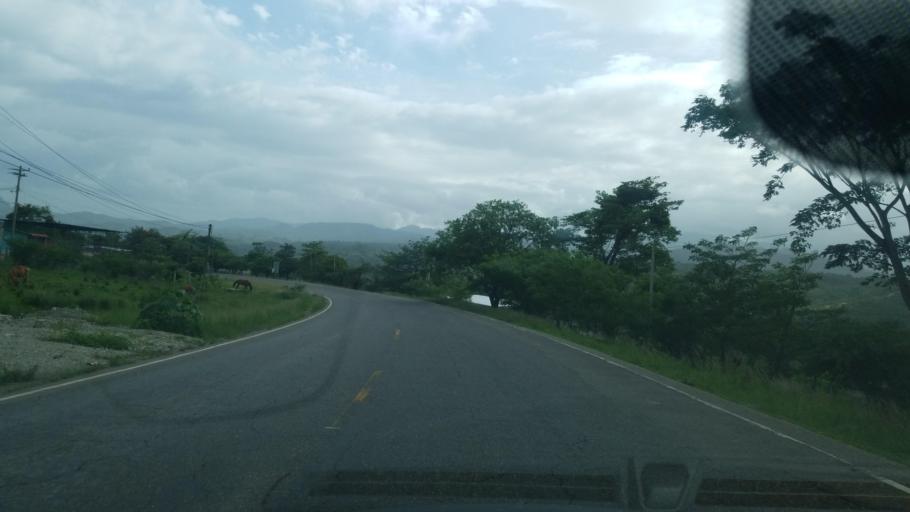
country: HN
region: Ocotepeque
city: Santa Lucia
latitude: 14.4182
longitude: -89.1929
